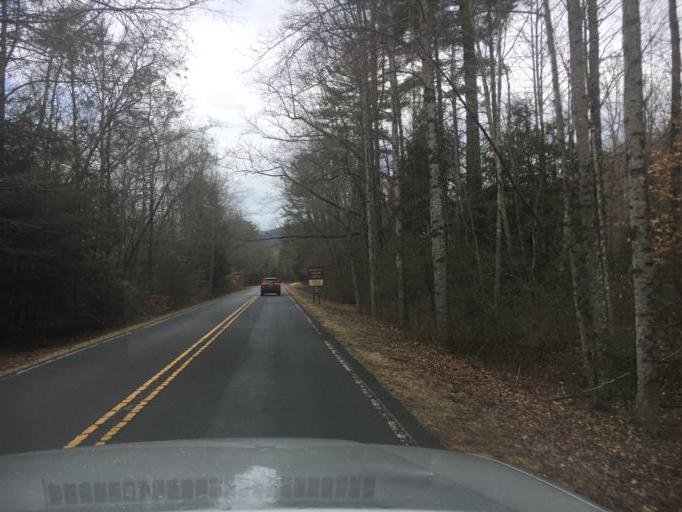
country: US
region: North Carolina
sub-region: Transylvania County
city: Brevard
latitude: 35.2836
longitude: -82.7239
